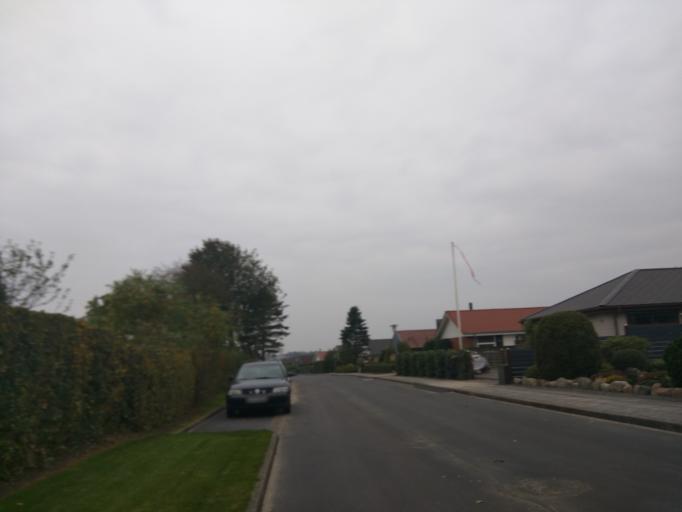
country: DK
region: Central Jutland
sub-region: Viborg Kommune
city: Viborg
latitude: 56.4565
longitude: 9.3861
